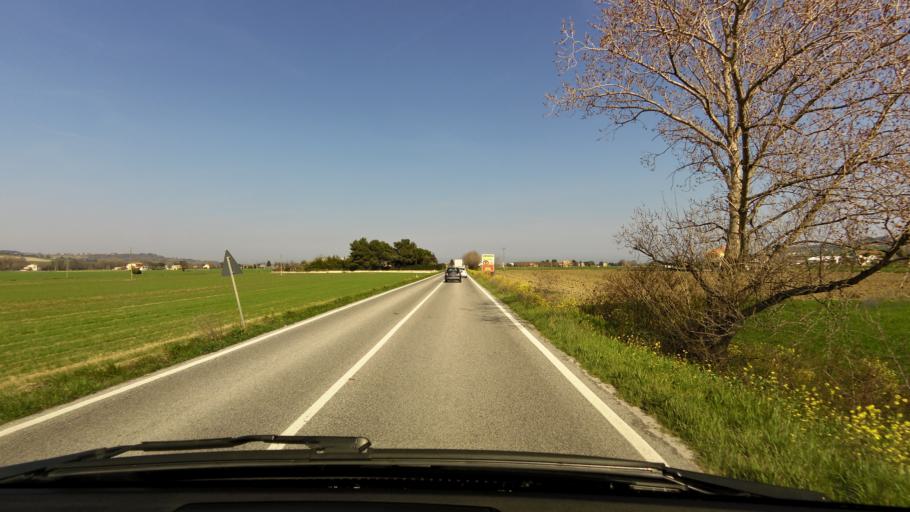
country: IT
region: The Marches
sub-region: Provincia di Macerata
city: Potenza Picena
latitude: 43.3842
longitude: 13.6183
